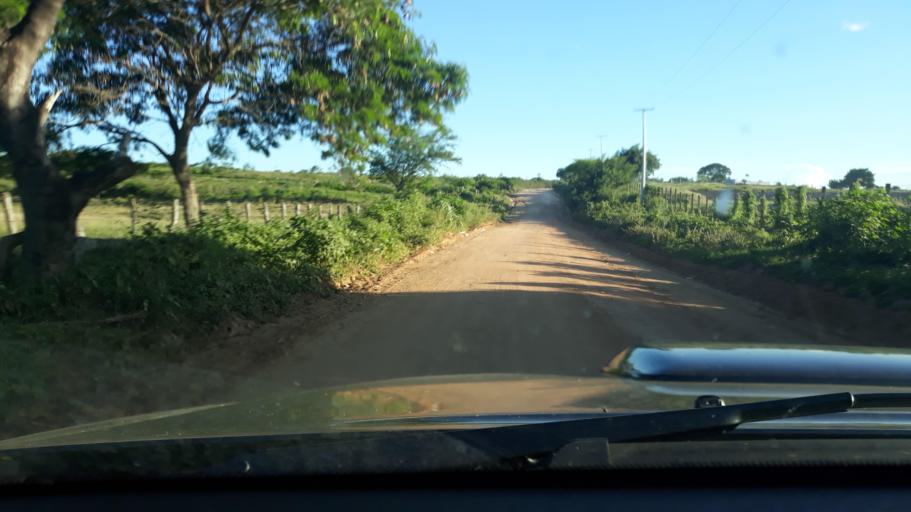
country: BR
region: Bahia
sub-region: Riacho De Santana
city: Riacho de Santana
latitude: -13.7891
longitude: -42.7126
